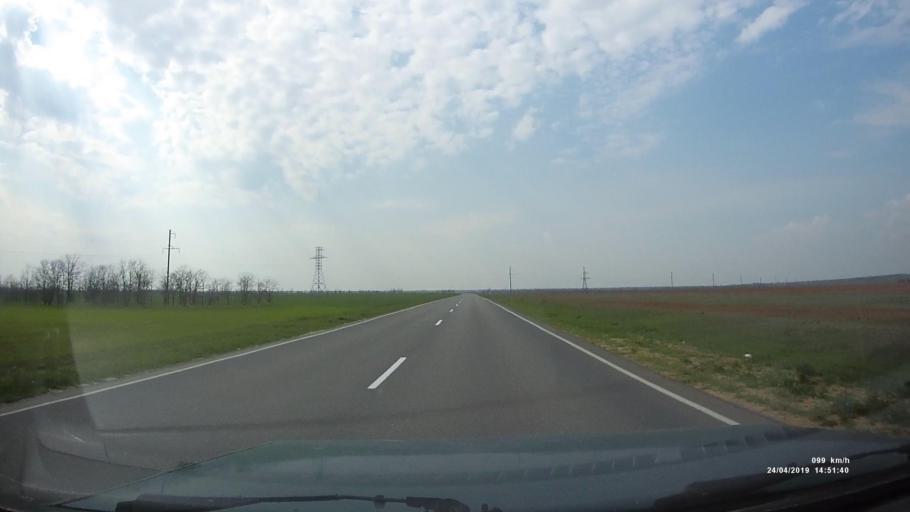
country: RU
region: Rostov
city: Remontnoye
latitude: 46.5265
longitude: 43.6964
